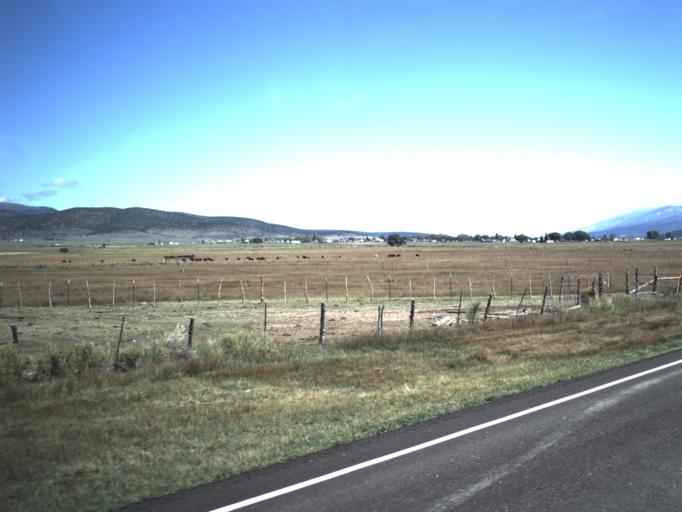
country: US
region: Utah
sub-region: Wayne County
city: Loa
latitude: 38.4857
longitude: -111.8887
